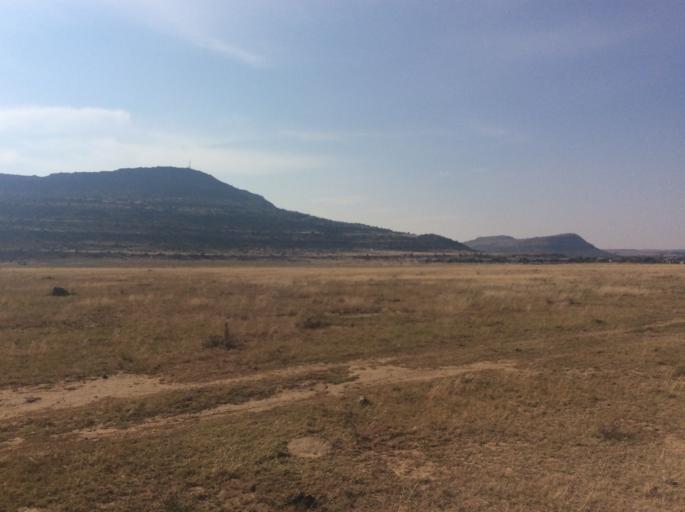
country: LS
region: Mafeteng
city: Mafeteng
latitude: -29.7072
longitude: 27.0085
